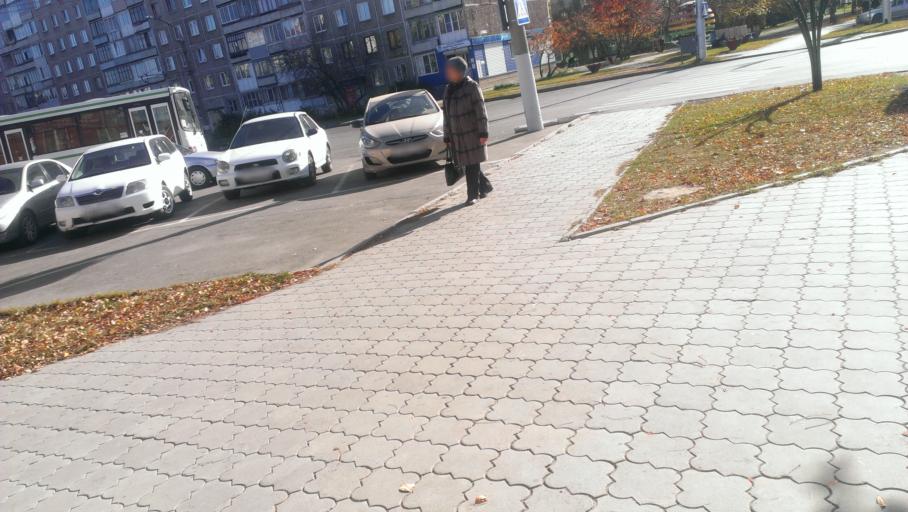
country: RU
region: Altai Krai
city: Novosilikatnyy
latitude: 53.3550
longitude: 83.6846
